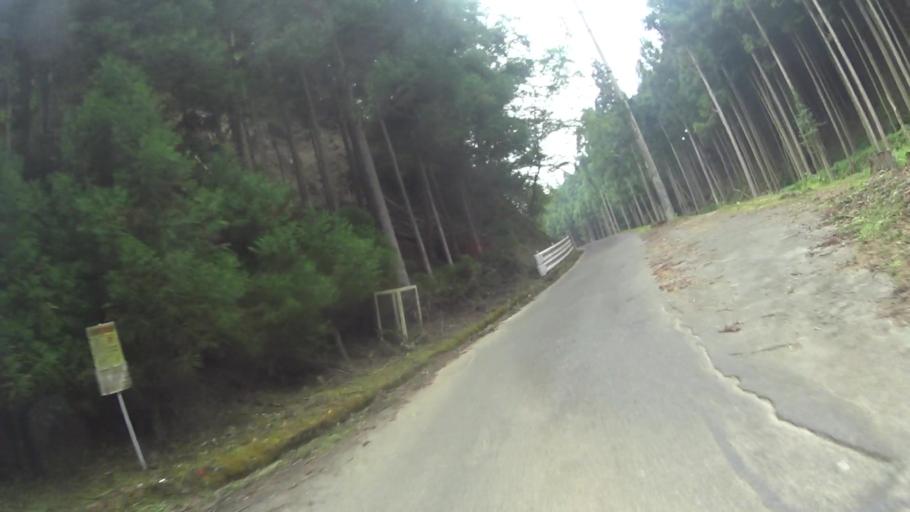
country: JP
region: Kyoto
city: Kameoka
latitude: 35.1656
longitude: 135.5650
